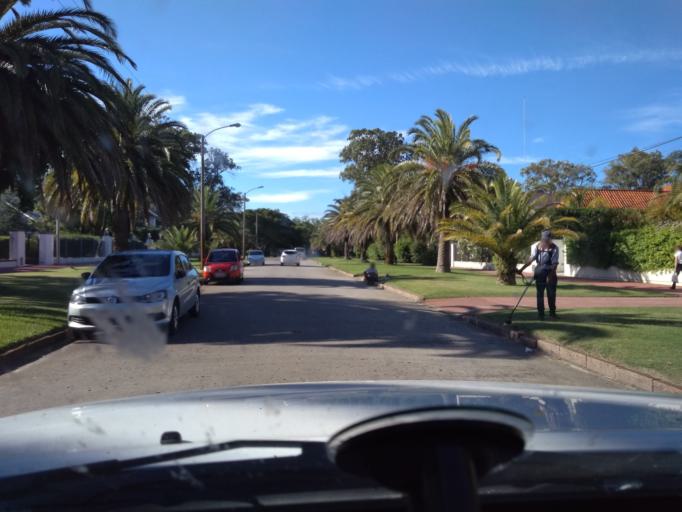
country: UY
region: Canelones
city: Paso de Carrasco
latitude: -34.8885
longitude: -56.0618
